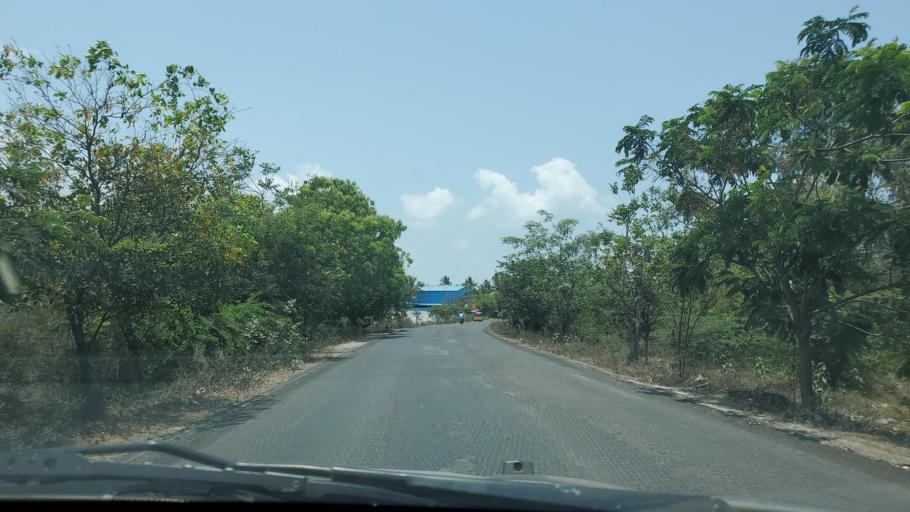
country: IN
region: Tamil Nadu
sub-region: Kancheepuram
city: Vengavasal
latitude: 12.8774
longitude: 80.1703
